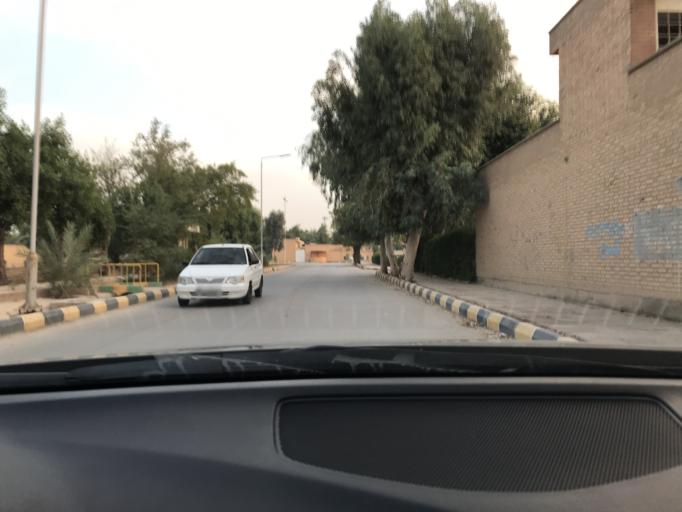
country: IR
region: Khuzestan
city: Ahvaz
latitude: 31.3305
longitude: 48.7357
